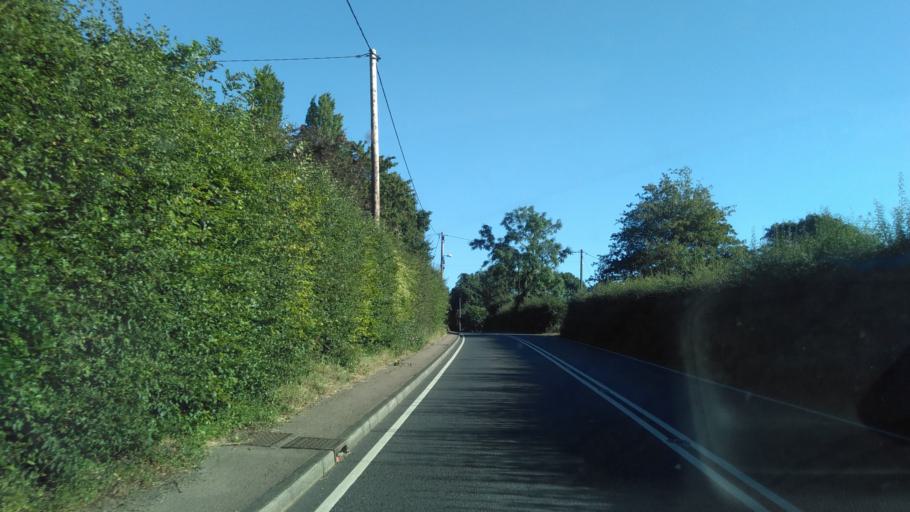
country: GB
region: England
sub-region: Kent
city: Blean
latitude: 51.3158
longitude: 1.0342
